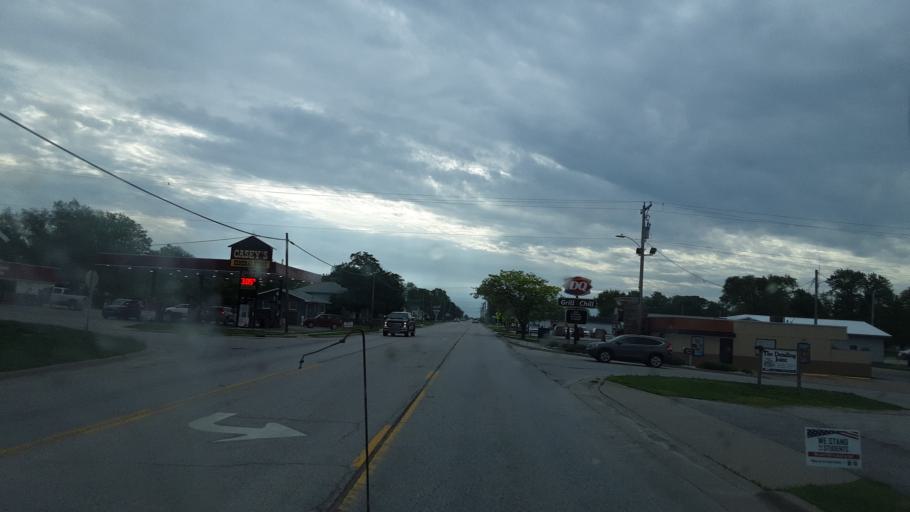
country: US
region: Illinois
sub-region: Hancock County
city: Hamilton
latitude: 40.3963
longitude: -91.3324
